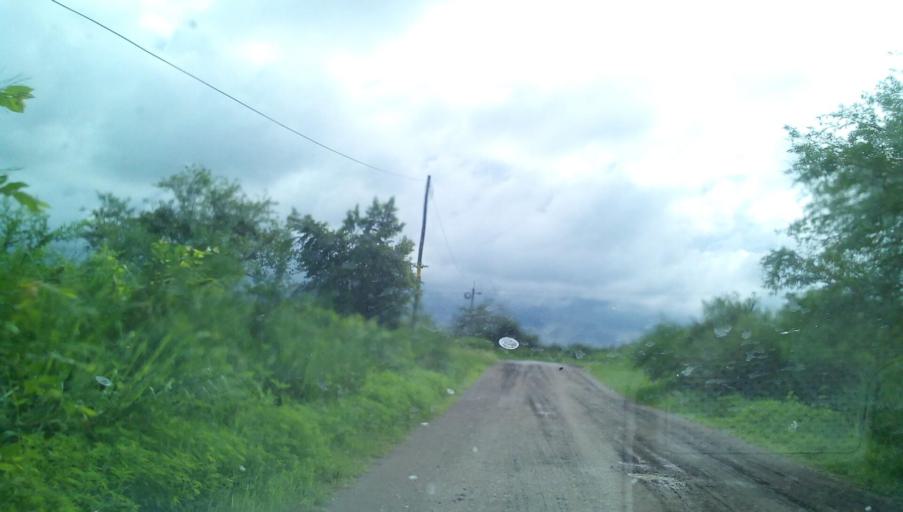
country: MX
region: Veracruz
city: Panuco
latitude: 21.8501
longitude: -98.1566
